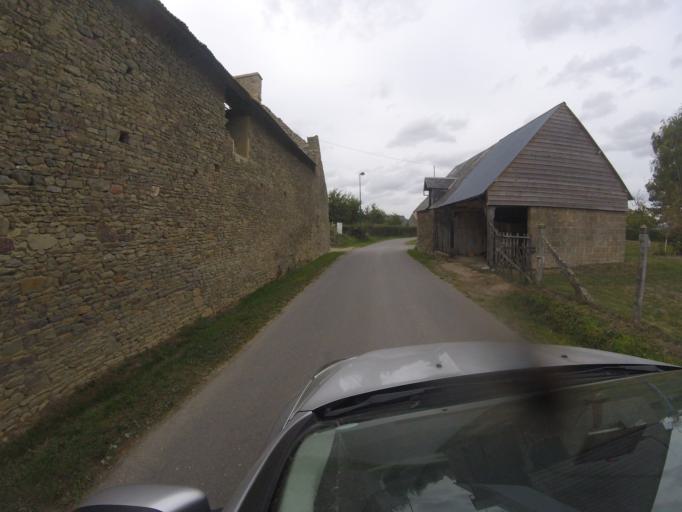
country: FR
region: Lower Normandy
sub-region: Departement de la Manche
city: Le Val-Saint-Pere
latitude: 48.6324
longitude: -1.3873
